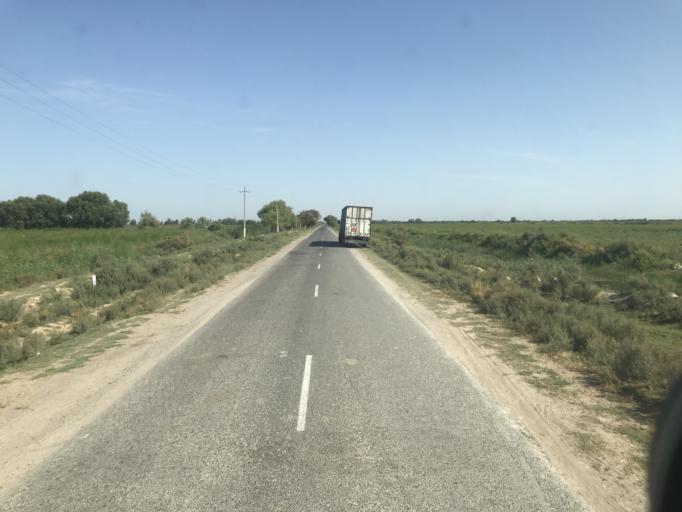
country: KZ
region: Ongtustik Qazaqstan
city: Myrzakent
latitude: 40.6688
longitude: 68.6333
